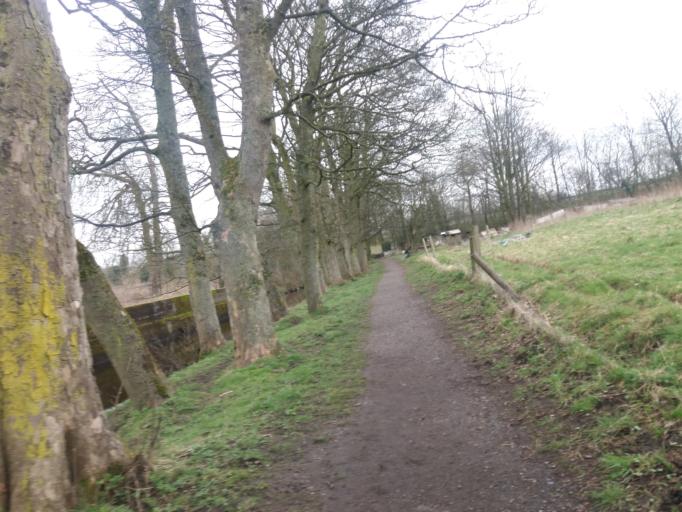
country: GB
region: England
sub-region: Lancashire
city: Chorley
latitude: 53.6586
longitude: -2.6127
